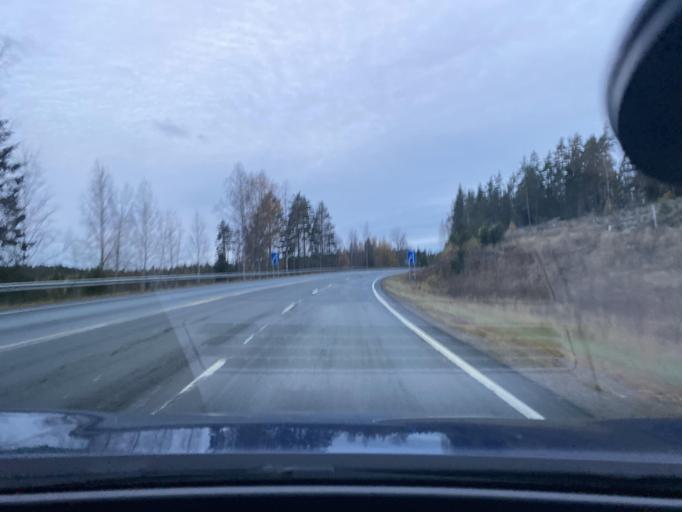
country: FI
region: Uusimaa
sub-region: Helsinki
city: Sammatti
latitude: 60.3827
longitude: 23.7528
